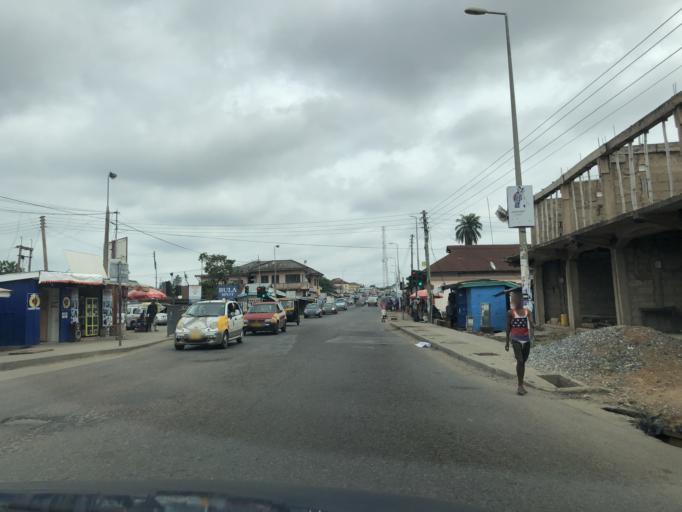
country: GH
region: Eastern
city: Koforidua
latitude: 6.0978
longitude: -0.2625
